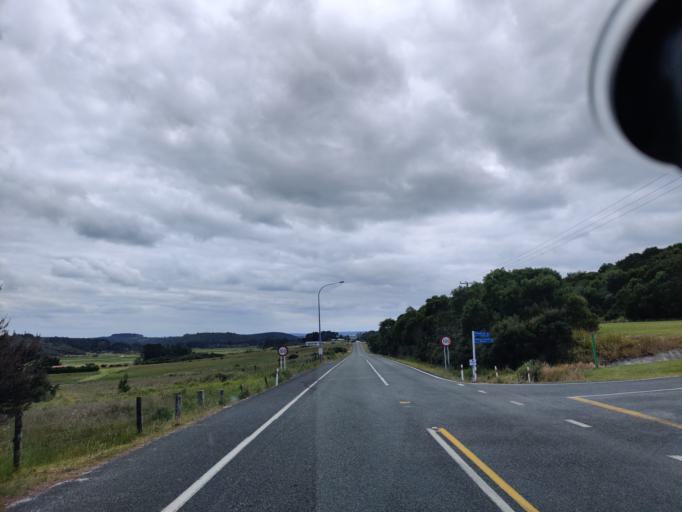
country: NZ
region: Northland
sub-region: Far North District
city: Kaitaia
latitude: -34.6498
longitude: 172.9702
